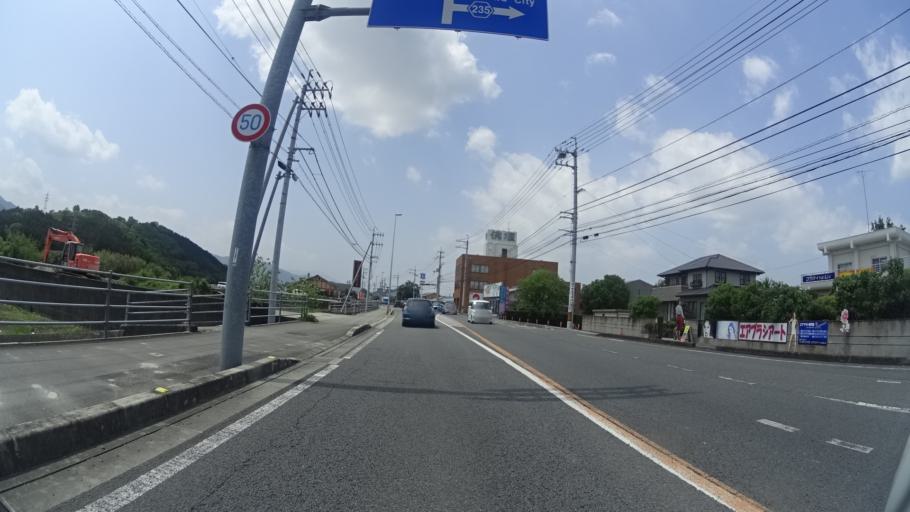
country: JP
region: Tokushima
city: Kamojimacho-jogejima
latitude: 34.0737
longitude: 134.3905
